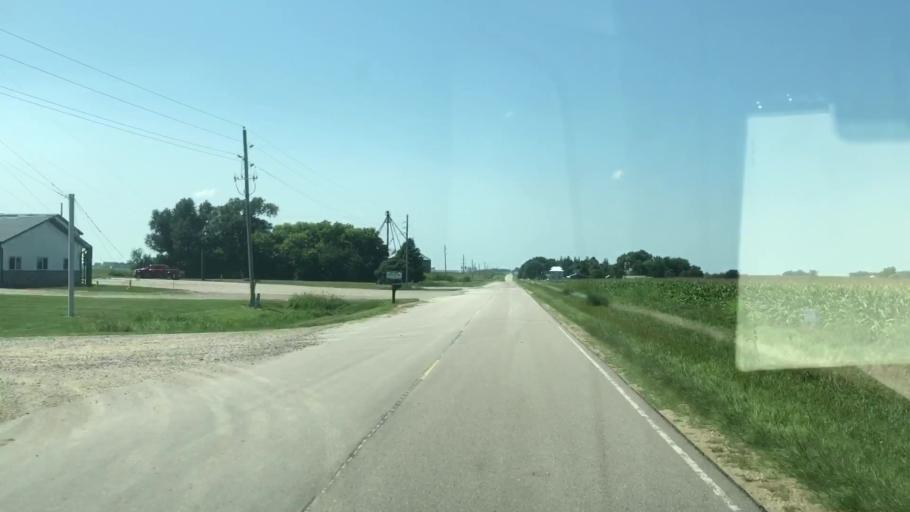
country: US
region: Iowa
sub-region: O'Brien County
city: Sheldon
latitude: 43.2443
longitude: -95.7747
